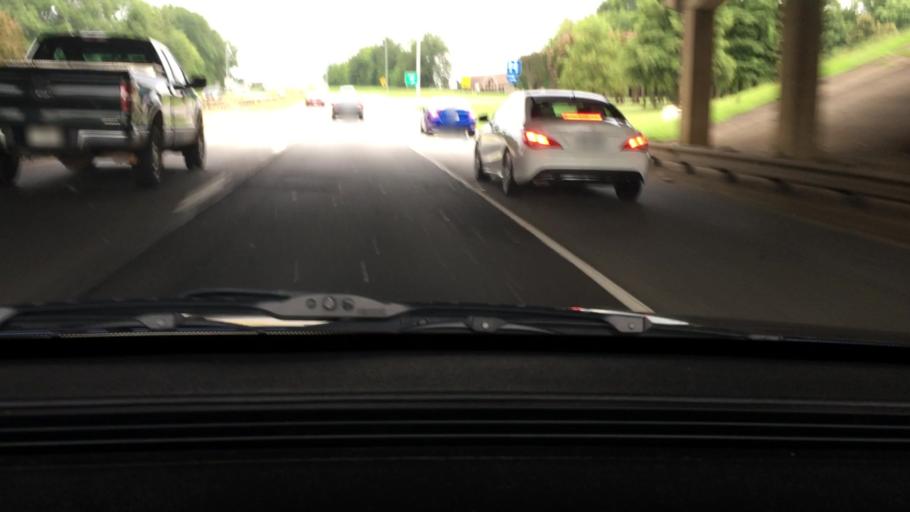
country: US
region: Alabama
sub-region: Tuscaloosa County
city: Tuscaloosa
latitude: 33.2062
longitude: -87.5245
